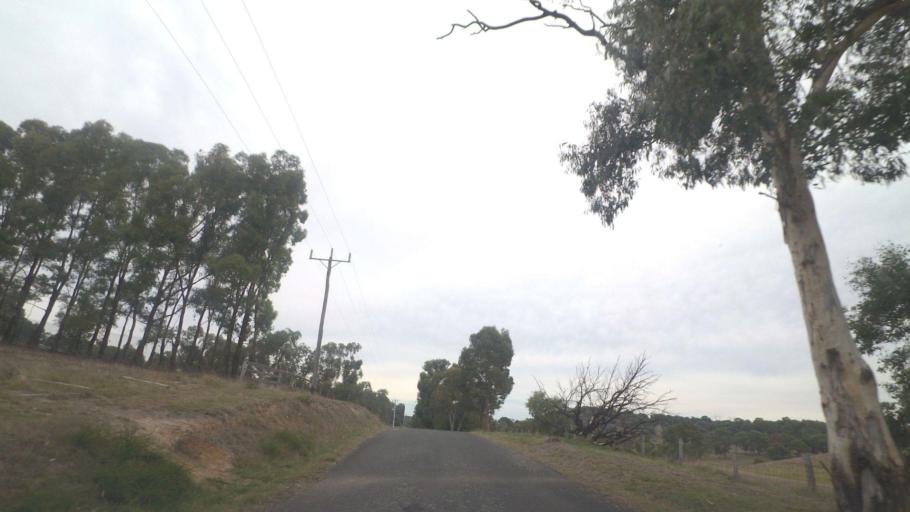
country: AU
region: Victoria
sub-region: Nillumbik
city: North Warrandyte
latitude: -37.7371
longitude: 145.1858
